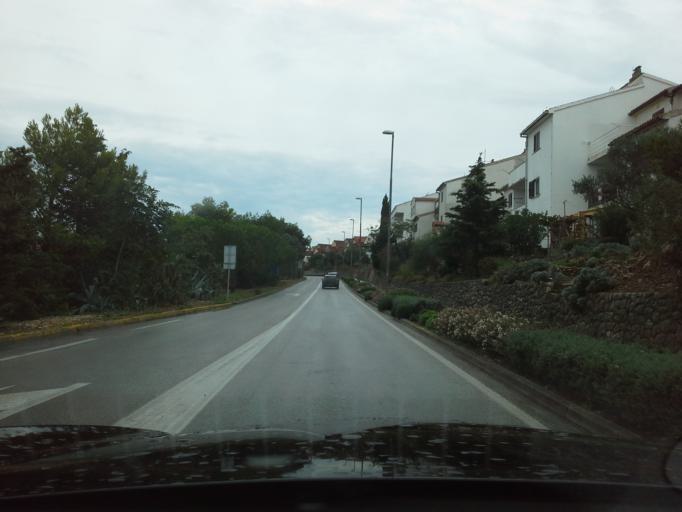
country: HR
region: Primorsko-Goranska
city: Mali Losinj
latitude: 44.5336
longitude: 14.4727
